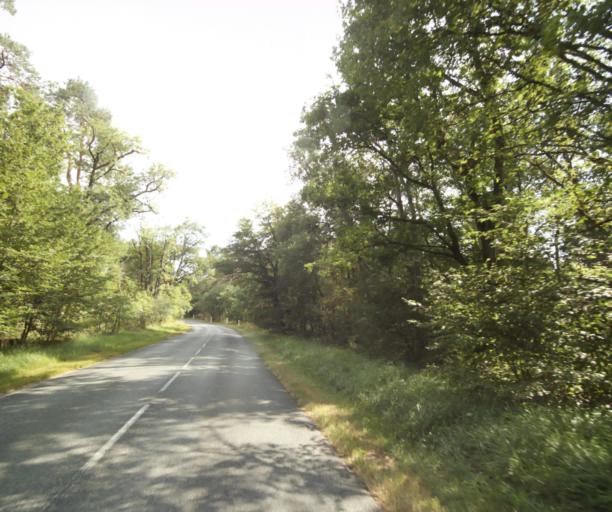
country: FR
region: Ile-de-France
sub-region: Departement de Seine-et-Marne
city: Acheres-la-Foret
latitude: 48.3723
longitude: 2.5606
